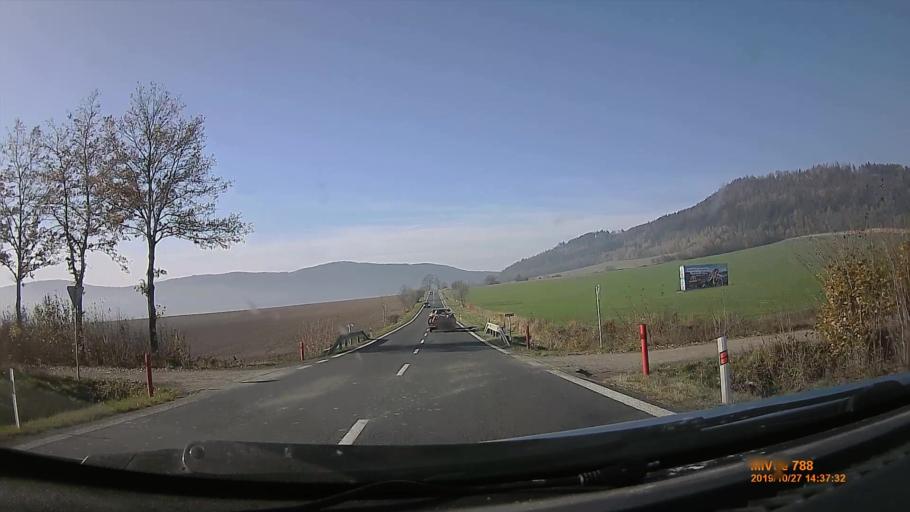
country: CZ
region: Olomoucky
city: Stity
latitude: 49.9911
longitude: 16.7855
